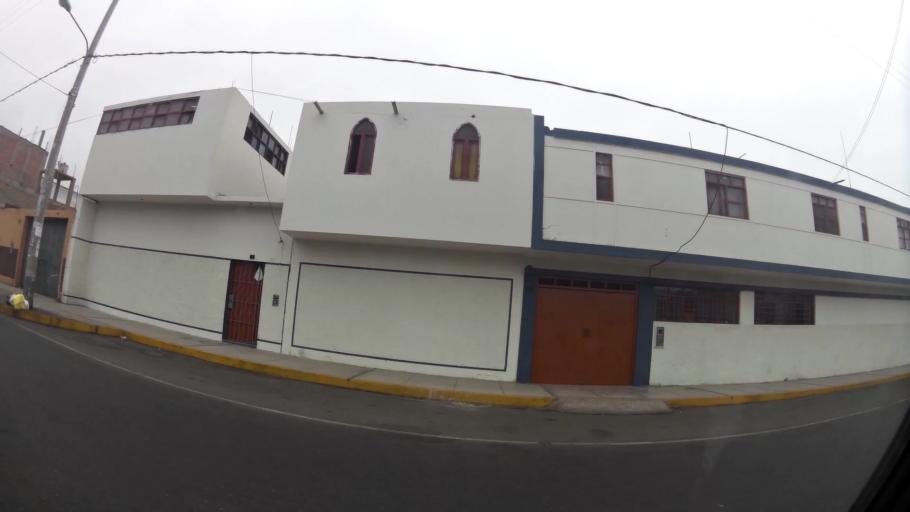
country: PE
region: Ancash
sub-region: Provincia de Santa
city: Chimbote
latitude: -9.0735
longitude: -78.5973
